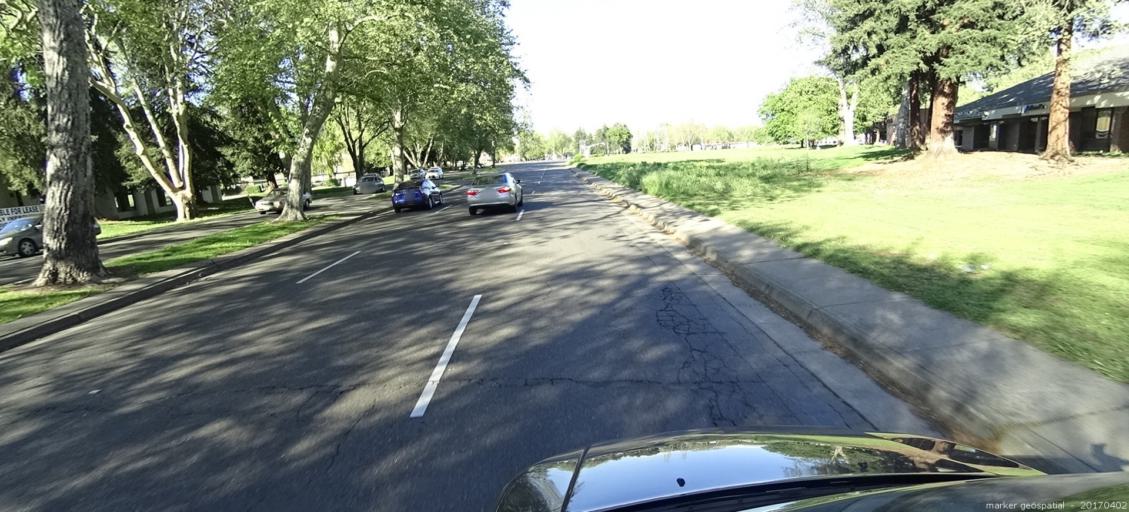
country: US
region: California
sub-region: Sacramento County
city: Arden-Arcade
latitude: 38.5718
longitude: -121.4180
